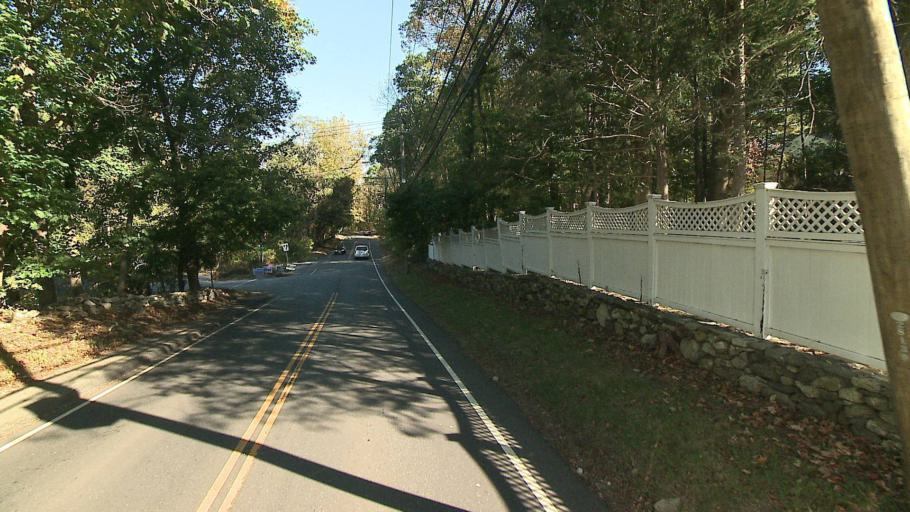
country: US
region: Connecticut
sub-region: Fairfield County
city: Westport
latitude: 41.1829
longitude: -73.3436
